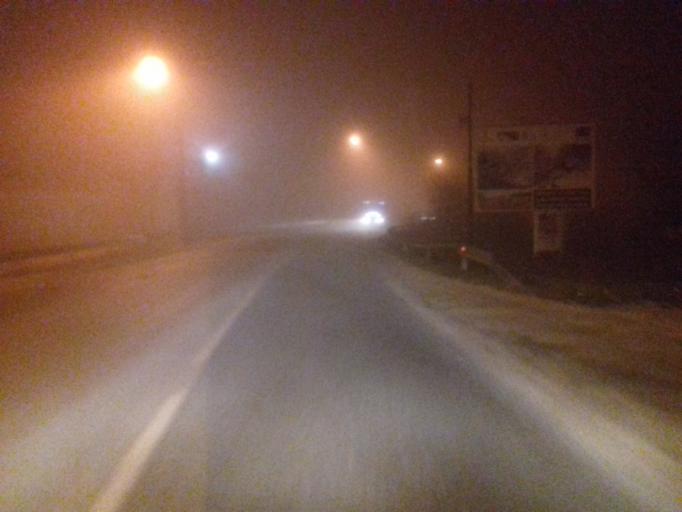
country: BA
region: Federation of Bosnia and Herzegovina
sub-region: Kanton Sarajevo
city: Sarajevo
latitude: 43.7776
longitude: 18.3623
